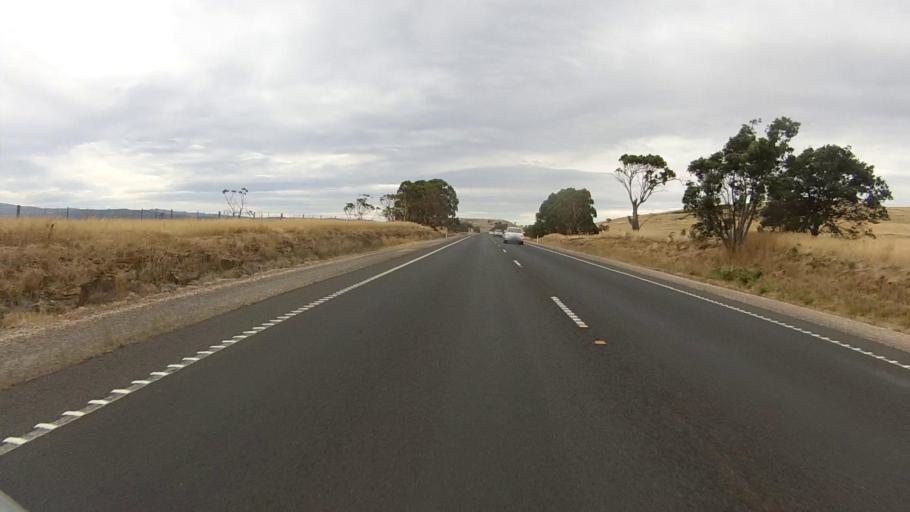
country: AU
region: Tasmania
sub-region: Brighton
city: Bridgewater
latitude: -42.3580
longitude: 147.3365
